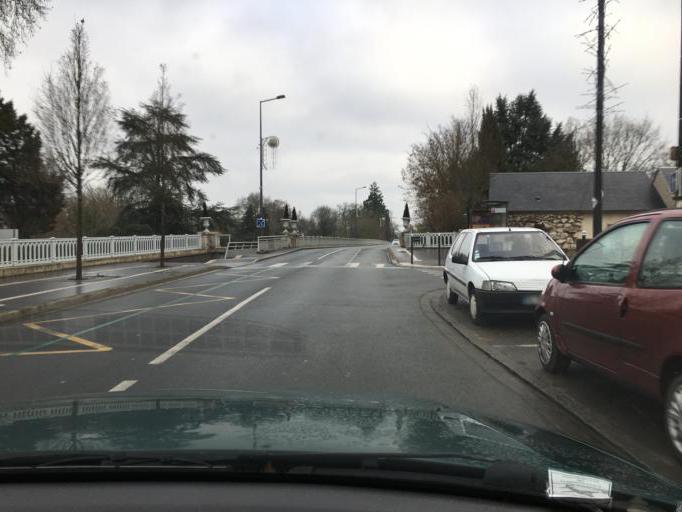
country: FR
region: Centre
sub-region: Departement du Loiret
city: Olivet
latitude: 47.8674
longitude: 1.9017
